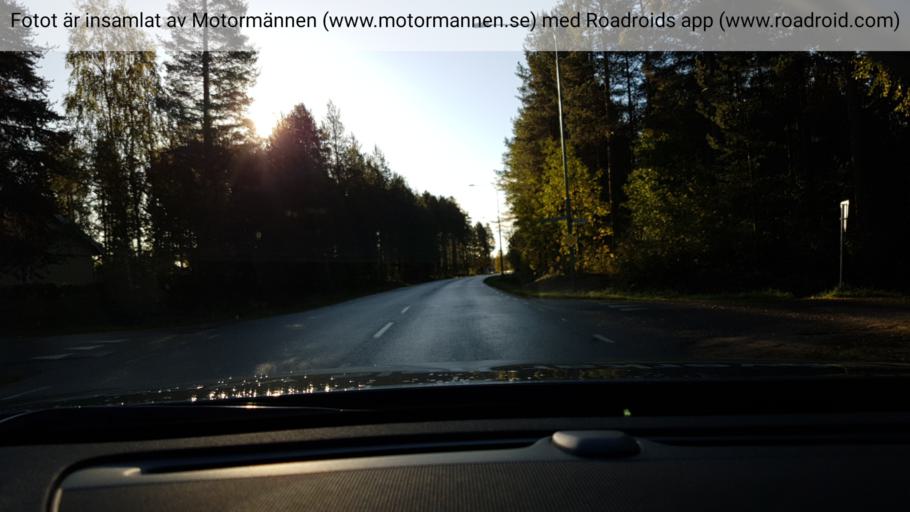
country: SE
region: Norrbotten
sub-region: Lulea Kommun
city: Sodra Sunderbyn
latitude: 65.6527
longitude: 21.9507
